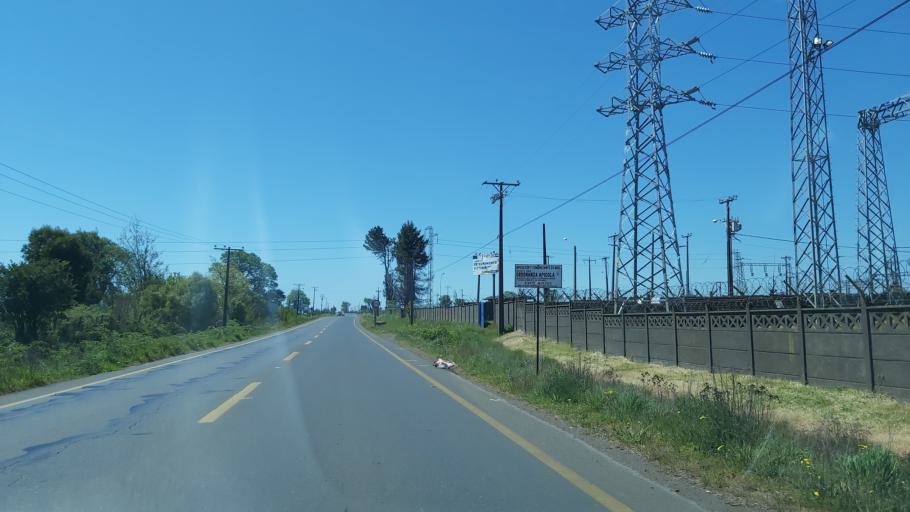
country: CL
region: Araucania
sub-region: Provincia de Malleco
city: Victoria
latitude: -38.2447
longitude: -72.3167
